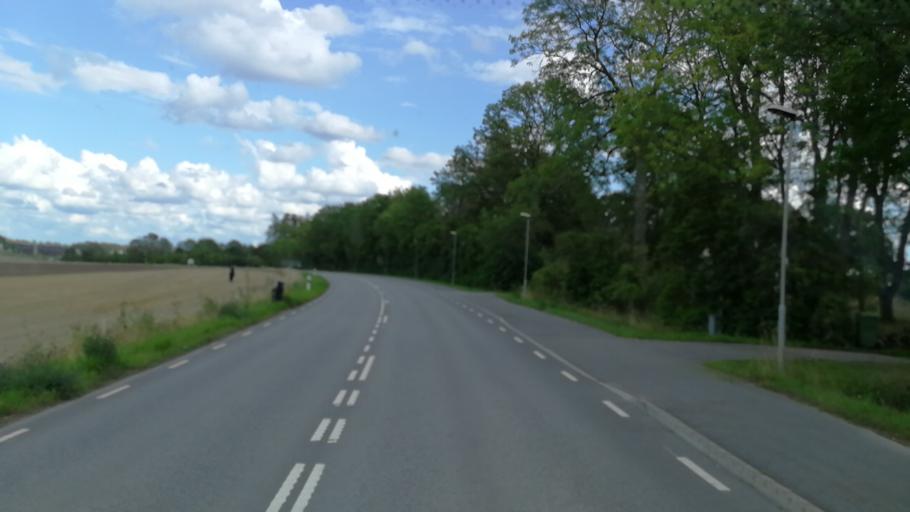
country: SE
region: OEstergoetland
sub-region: Linkopings Kommun
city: Ljungsbro
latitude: 58.4911
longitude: 15.4731
